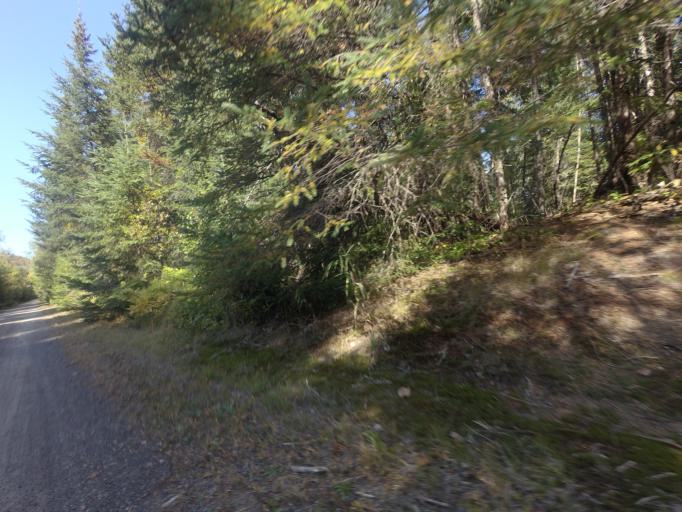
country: CA
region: Quebec
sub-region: Laurentides
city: Sainte-Agathe-des-Monts
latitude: 46.0801
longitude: -74.3268
